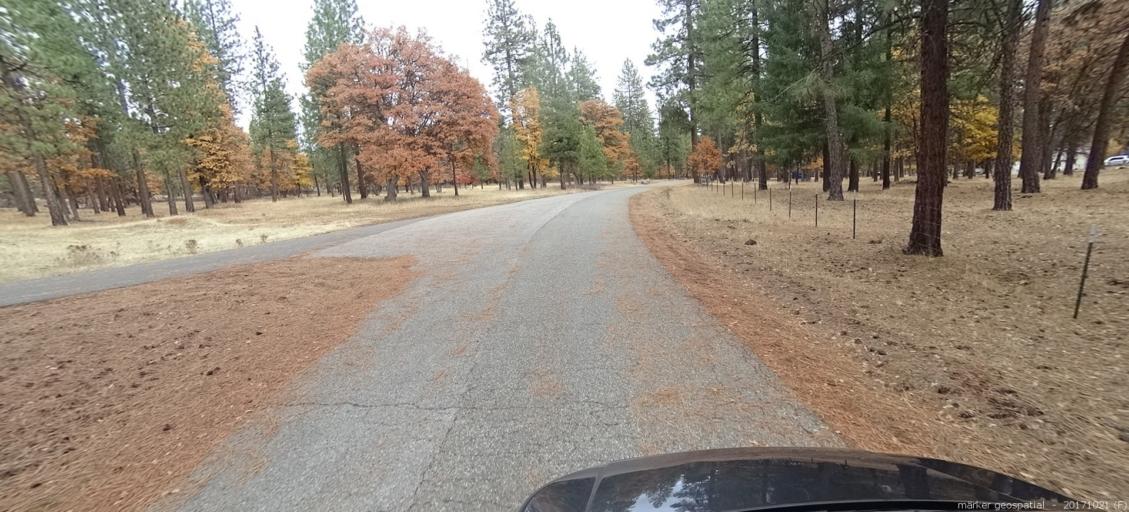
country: US
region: California
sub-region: Shasta County
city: Burney
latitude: 40.9275
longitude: -121.6580
